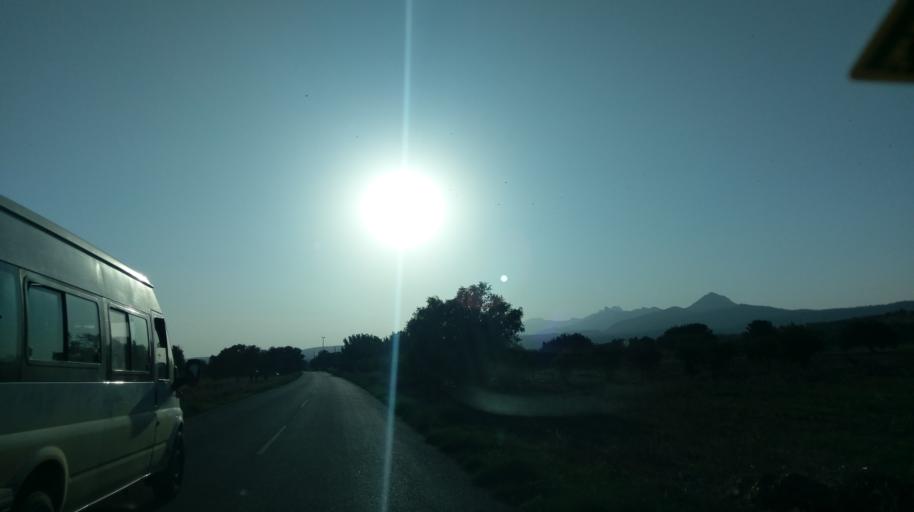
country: CY
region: Ammochostos
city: Leonarisso
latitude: 35.4291
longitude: 34.0152
